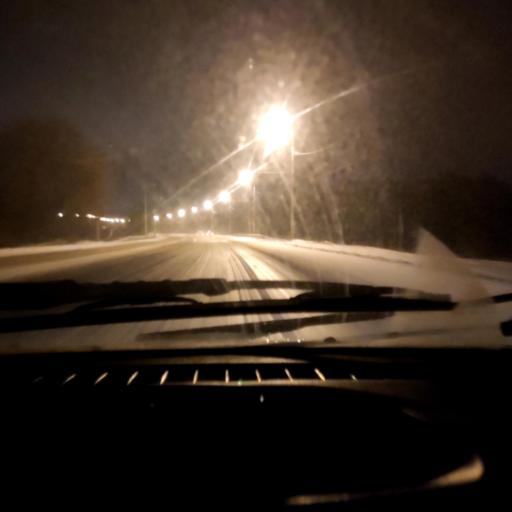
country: RU
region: Samara
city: Zhigulevsk
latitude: 53.4987
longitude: 49.5109
